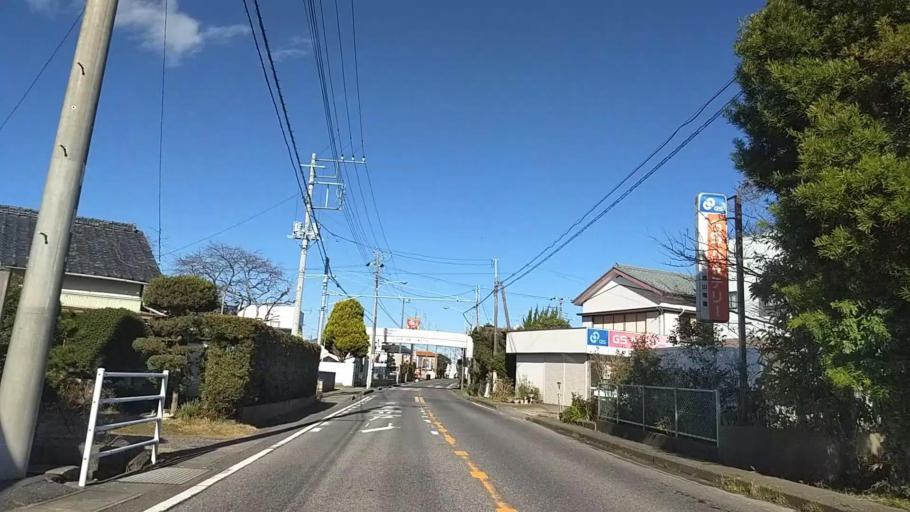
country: JP
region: Chiba
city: Ohara
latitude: 35.2456
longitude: 140.3938
